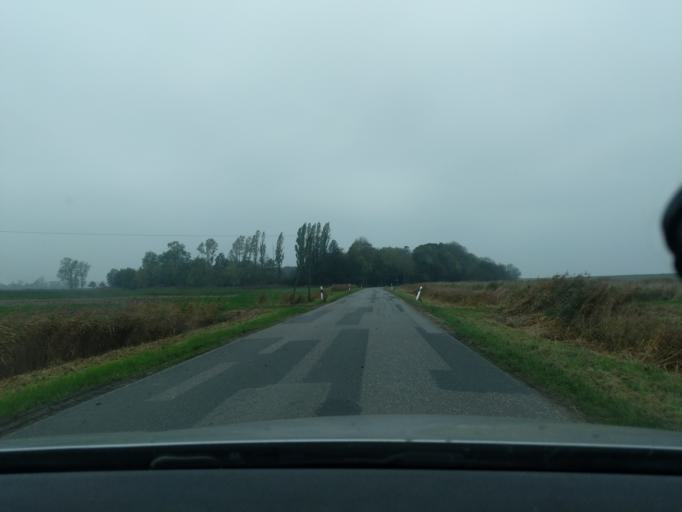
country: DE
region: Lower Saxony
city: Nordleda
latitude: 53.8263
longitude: 8.8298
